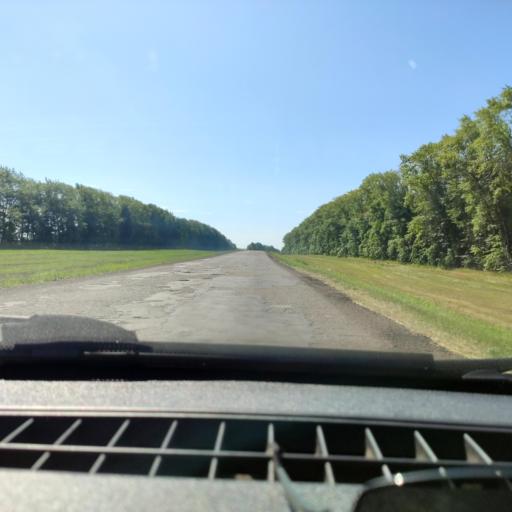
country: RU
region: Bashkortostan
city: Karmaskaly
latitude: 54.3915
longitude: 56.1732
